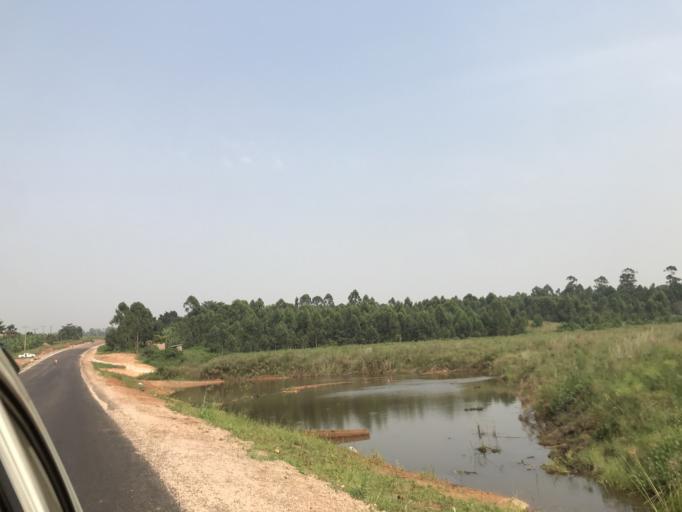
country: UG
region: Central Region
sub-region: Kalungu District
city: Kalungu
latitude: -0.2291
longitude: 31.7210
